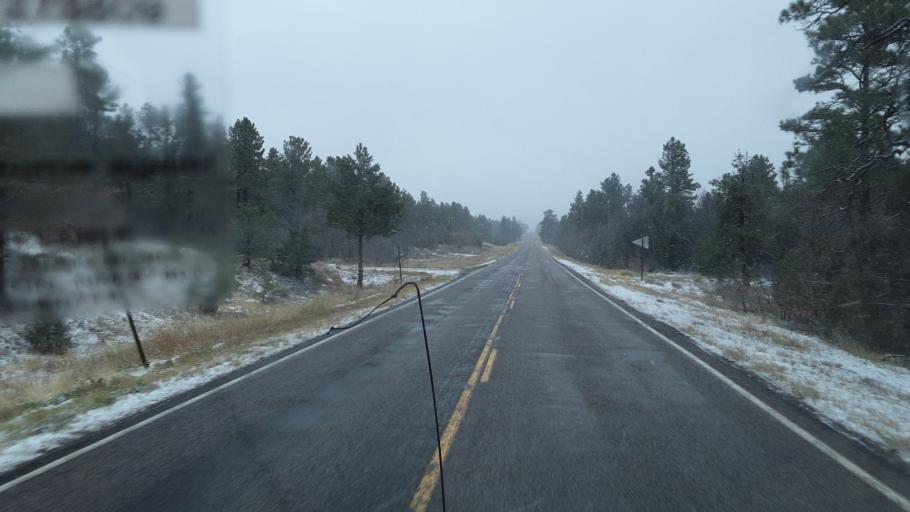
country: US
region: New Mexico
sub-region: Rio Arriba County
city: Tierra Amarilla
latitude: 36.6713
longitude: -106.5577
